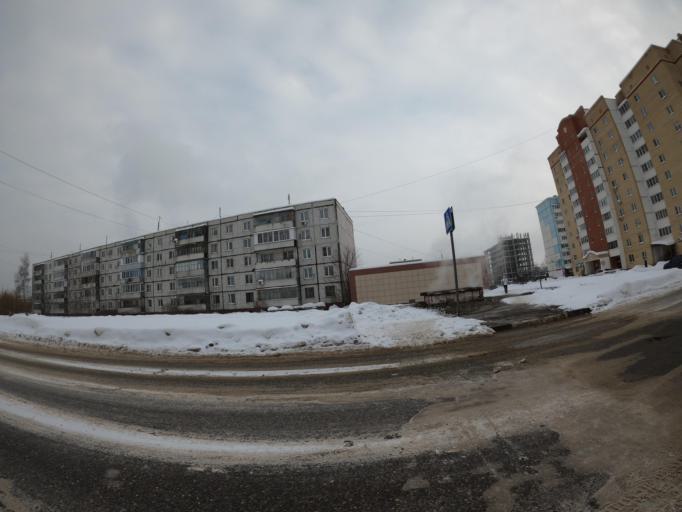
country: RU
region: Moskovskaya
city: Elektrogorsk
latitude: 55.8842
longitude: 38.7746
